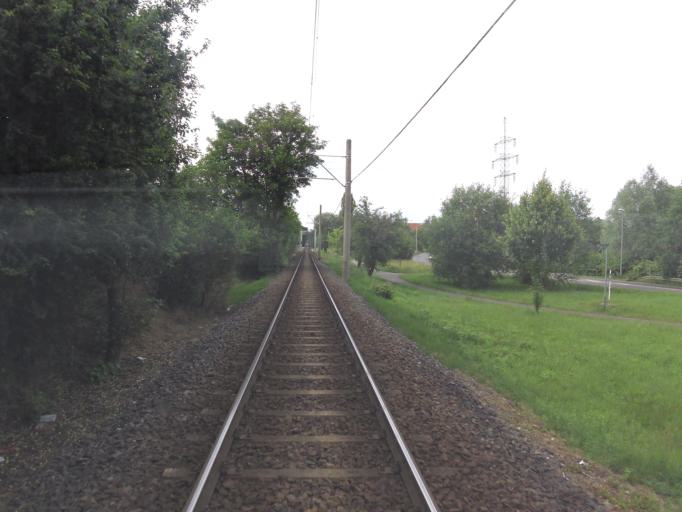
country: DE
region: Saxony
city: Markkleeberg
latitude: 51.2918
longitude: 12.3188
